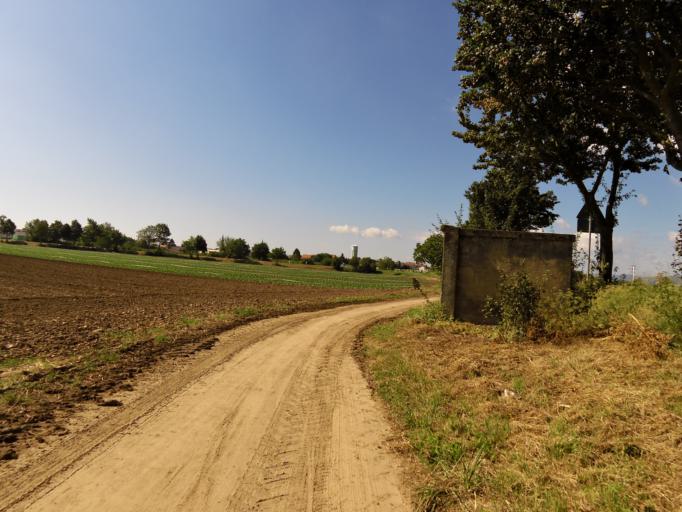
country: DE
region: Rheinland-Pfalz
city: Bohl-Iggelheim
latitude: 49.3937
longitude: 8.2974
